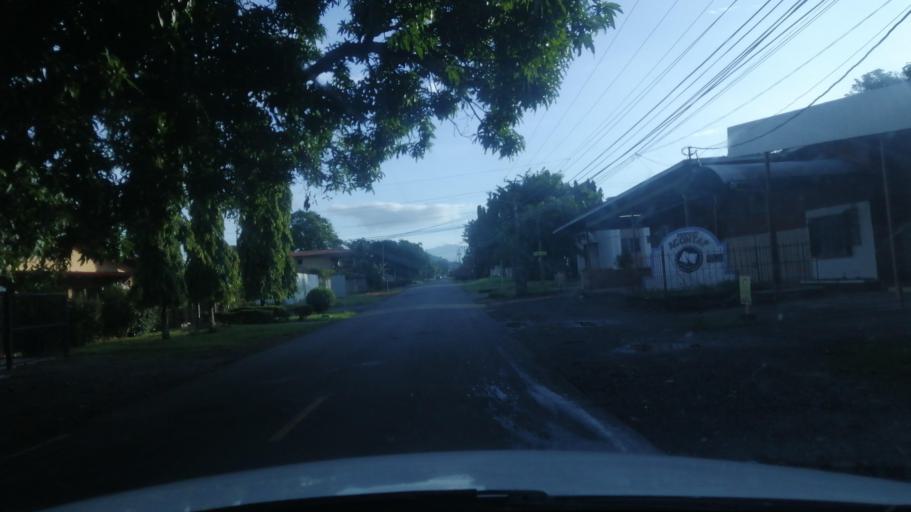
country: PA
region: Chiriqui
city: Mata del Nance
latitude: 8.4474
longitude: -82.4209
